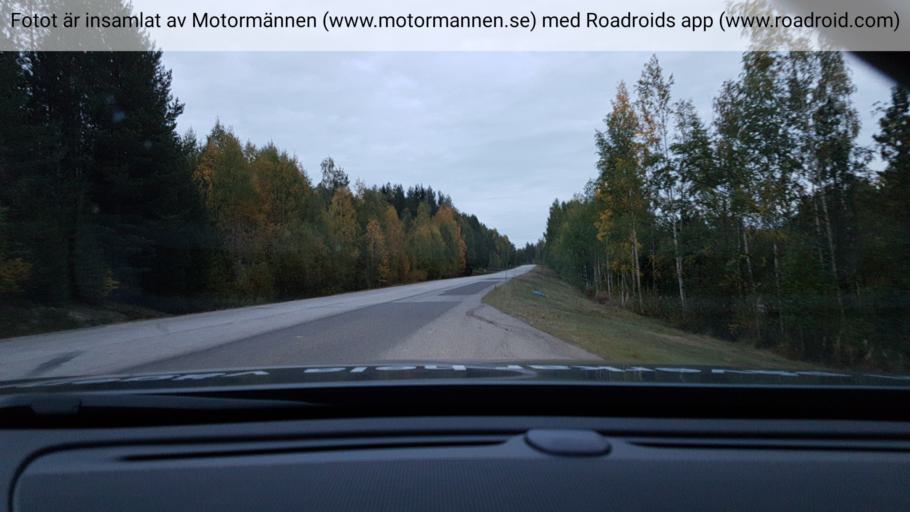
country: SE
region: Norrbotten
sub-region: Alvsbyns Kommun
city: AElvsbyn
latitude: 65.8525
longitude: 20.4494
